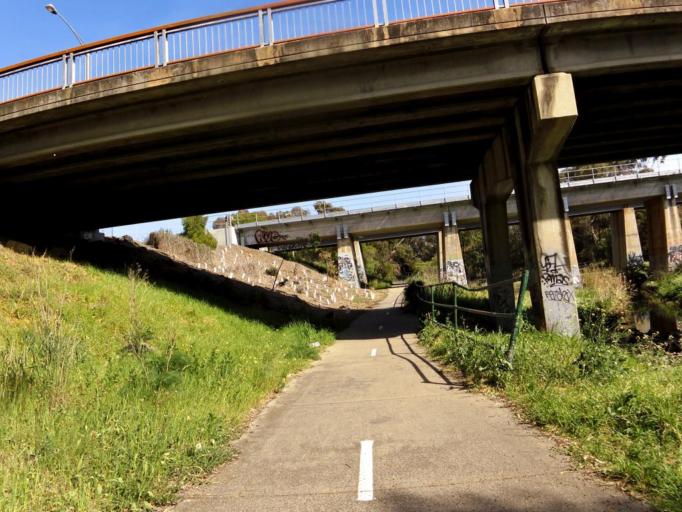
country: AU
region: Victoria
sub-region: Brimbank
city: Sunshine West
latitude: -37.7839
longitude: 144.8155
